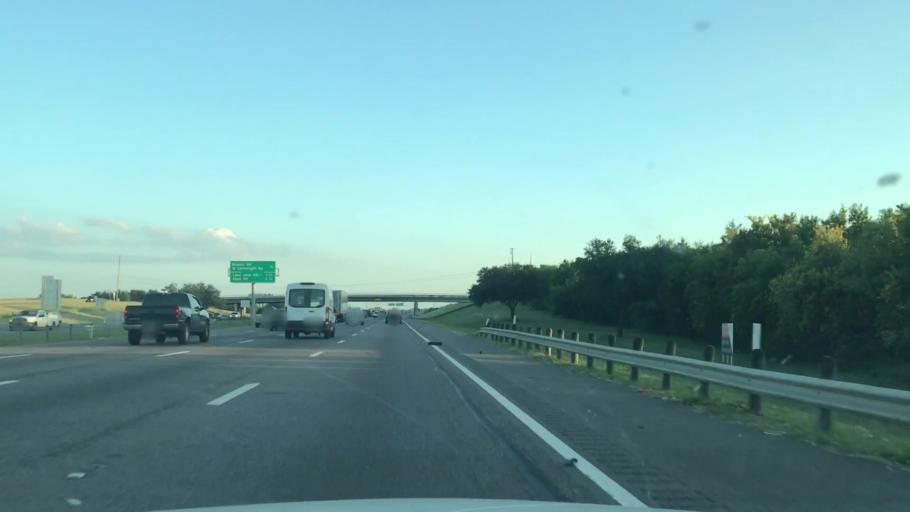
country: US
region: Texas
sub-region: Dallas County
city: Mesquite
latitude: 32.7582
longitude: -96.6186
